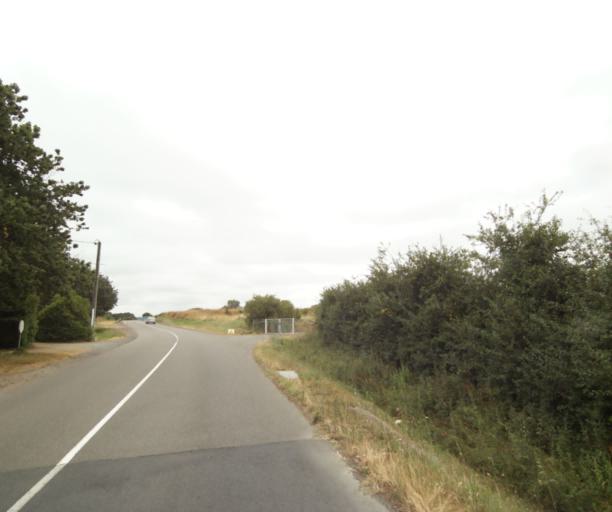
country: FR
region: Pays de la Loire
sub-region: Departement de la Vendee
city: Chateau-d'Olonne
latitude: 46.5136
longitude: -1.7391
